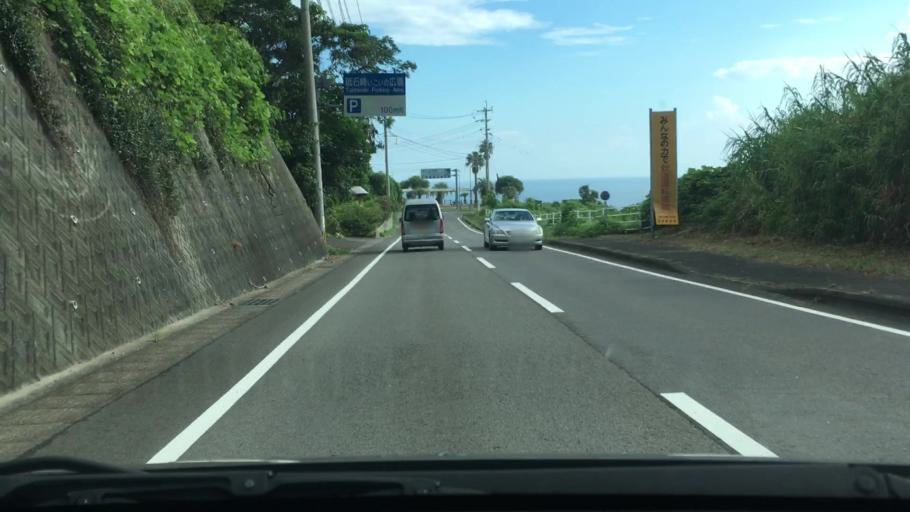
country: JP
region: Nagasaki
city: Togitsu
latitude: 32.8462
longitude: 129.6945
